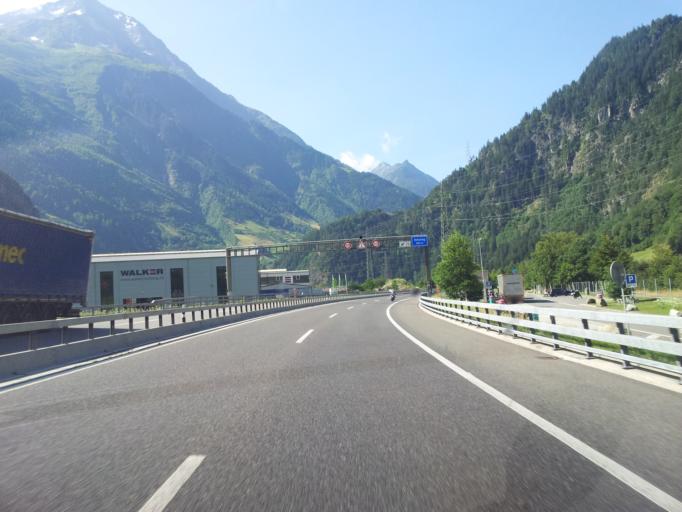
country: CH
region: Uri
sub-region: Uri
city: Silenen
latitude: 46.7819
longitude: 8.6688
